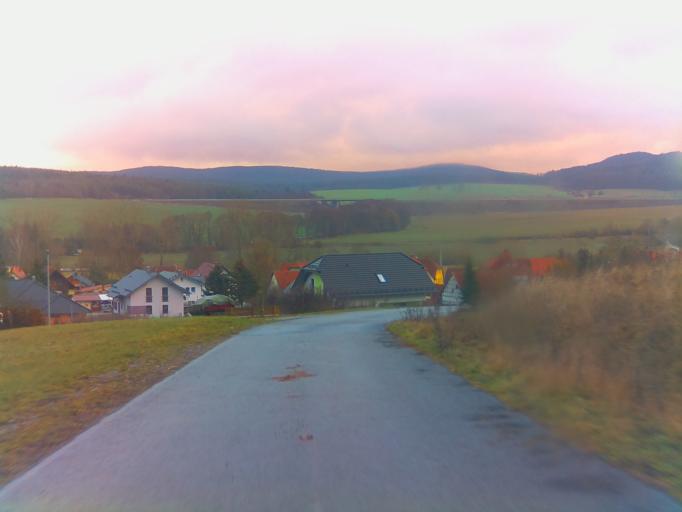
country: DE
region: Thuringia
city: Wolfershausen
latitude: 50.4685
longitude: 10.4343
